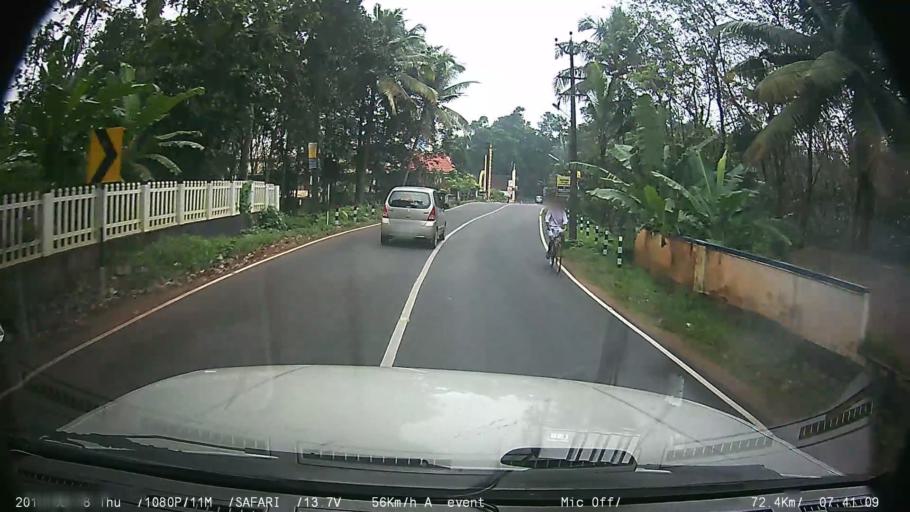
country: IN
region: Kerala
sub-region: Kottayam
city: Changanacheri
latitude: 9.4578
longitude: 76.5763
